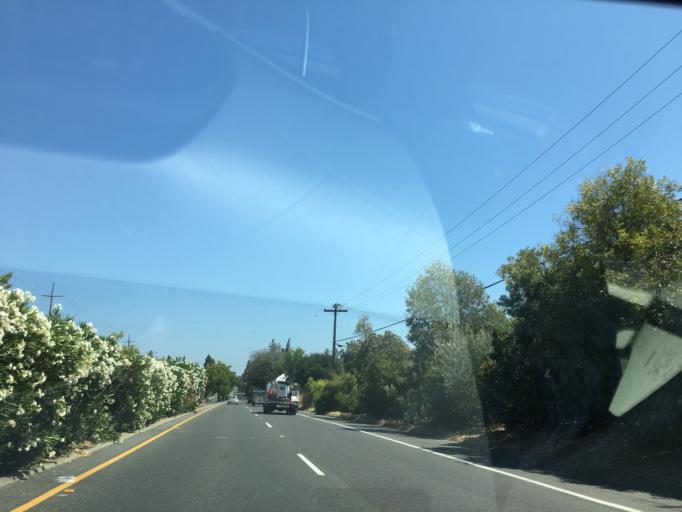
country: US
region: California
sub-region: Santa Clara County
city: Loyola
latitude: 37.3665
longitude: -122.1055
